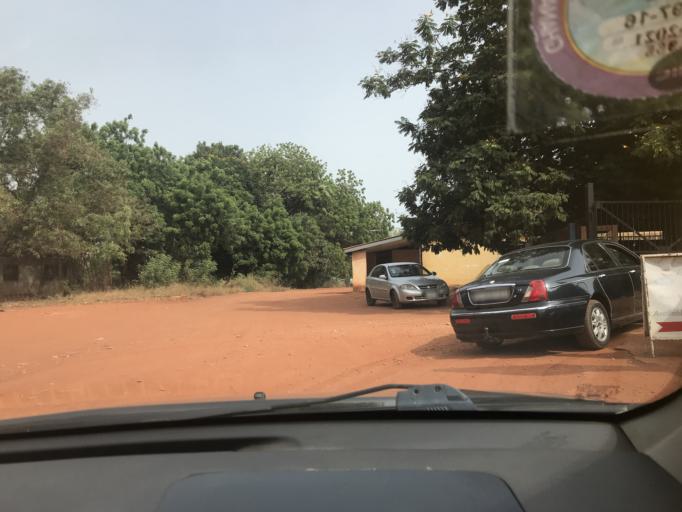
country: GH
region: Greater Accra
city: Teshi Old Town
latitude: 5.5891
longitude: -0.1569
